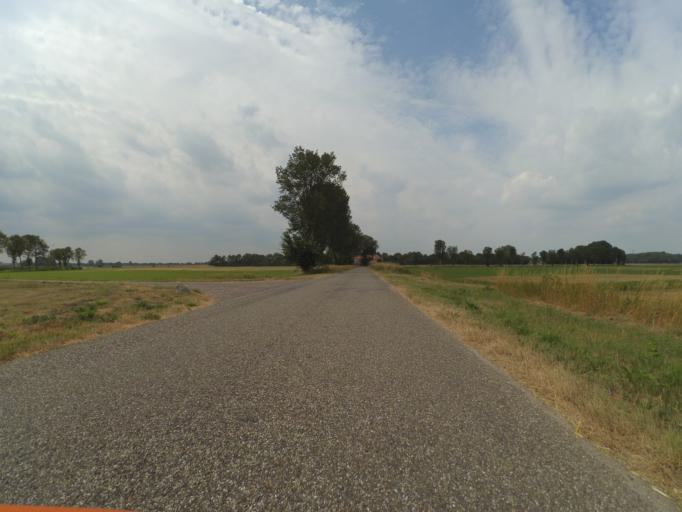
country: NL
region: Overijssel
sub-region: Gemeente Hof van Twente
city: Markelo
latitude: 52.1809
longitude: 6.4952
